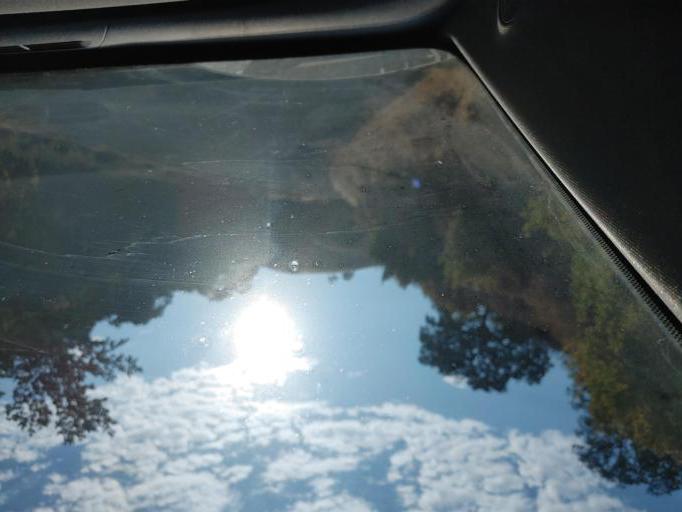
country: US
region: California
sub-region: San Benito County
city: Ridgemark
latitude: 36.7699
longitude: -121.2065
